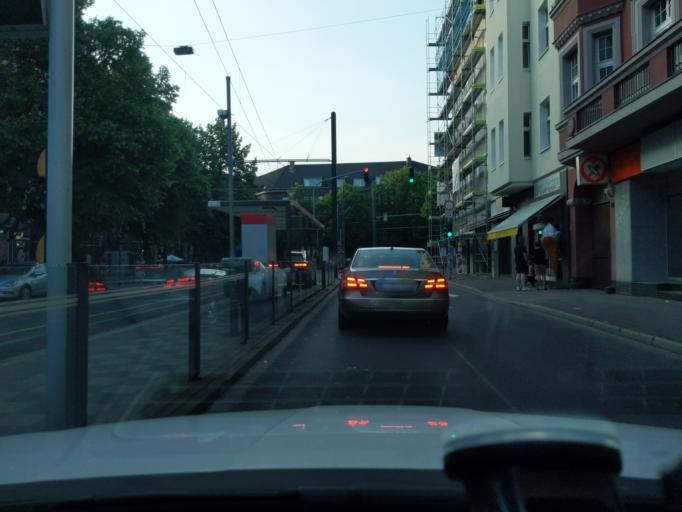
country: DE
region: North Rhine-Westphalia
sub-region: Regierungsbezirk Dusseldorf
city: Dusseldorf
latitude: 51.2051
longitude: 6.7803
